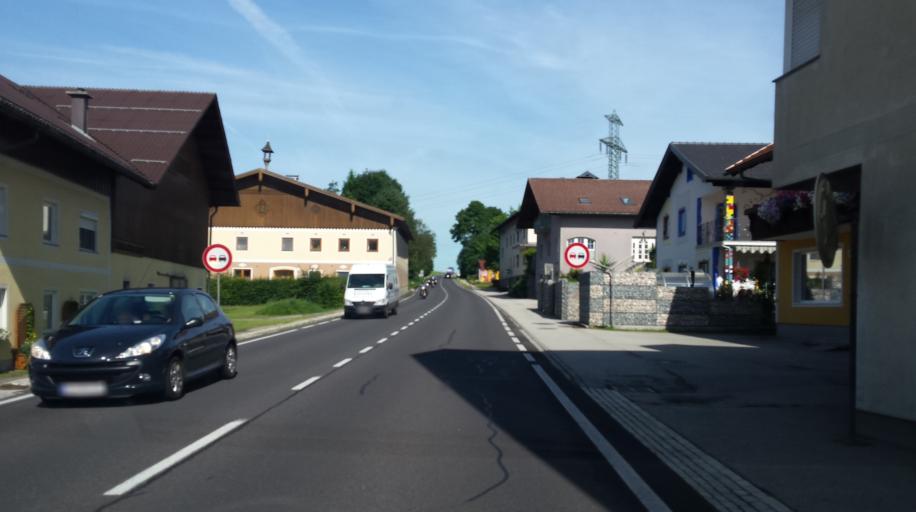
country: AT
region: Upper Austria
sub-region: Politischer Bezirk Vocklabruck
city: Frankenmarkt
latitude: 47.9941
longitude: 13.3509
